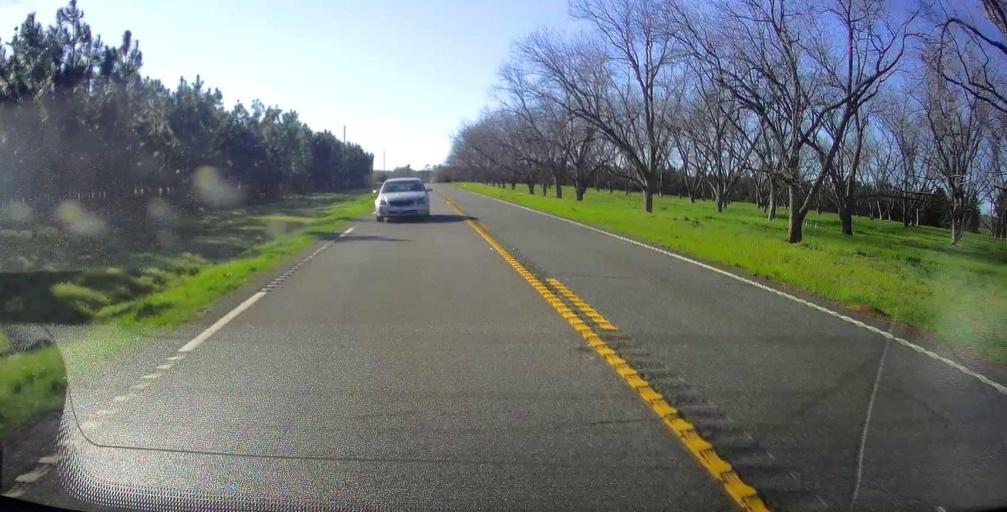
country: US
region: Georgia
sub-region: Macon County
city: Marshallville
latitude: 32.4452
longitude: -83.8996
